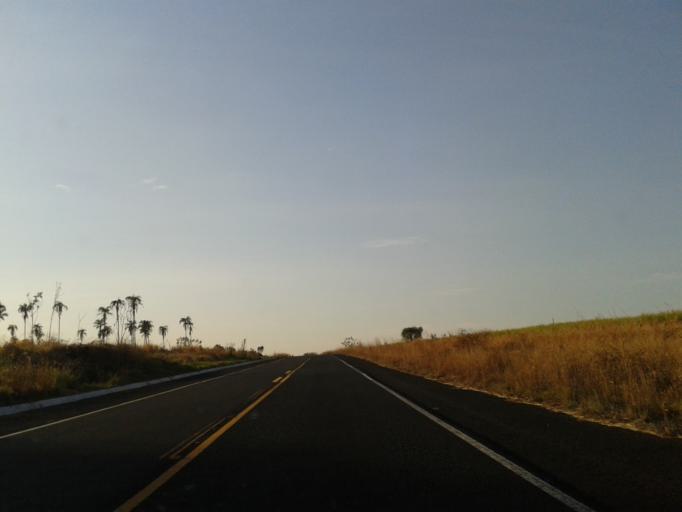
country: BR
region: Minas Gerais
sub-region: Santa Vitoria
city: Santa Vitoria
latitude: -19.1169
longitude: -50.3095
